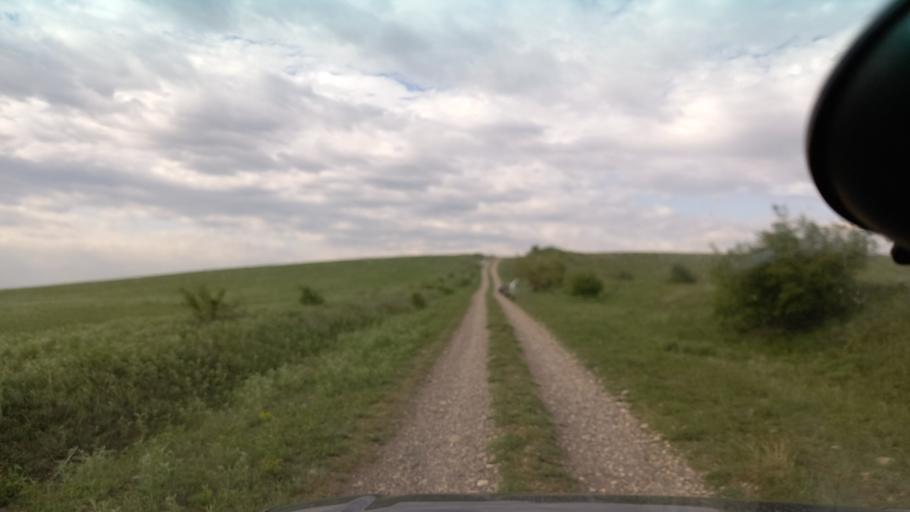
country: RU
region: Kabardino-Balkariya
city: Kuba-Taba
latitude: 43.8105
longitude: 43.4083
